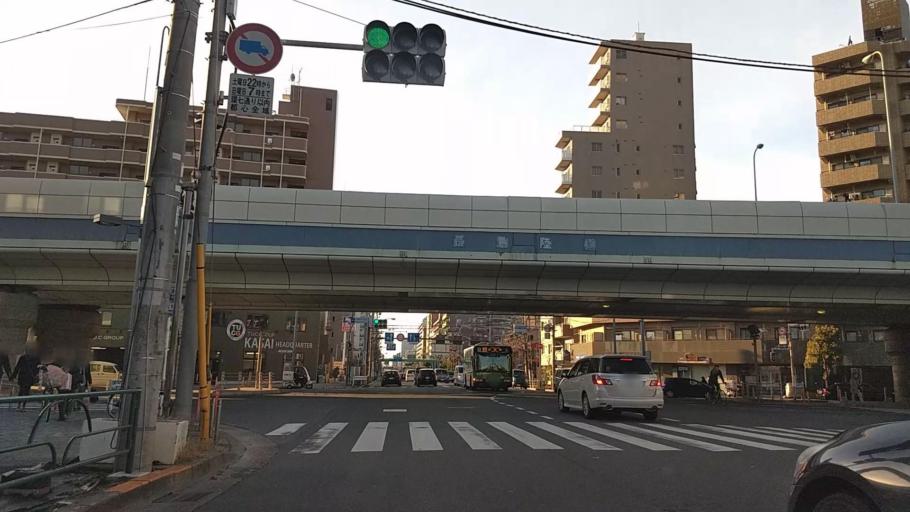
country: JP
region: Tokyo
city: Urayasu
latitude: 35.6675
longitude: 139.8737
